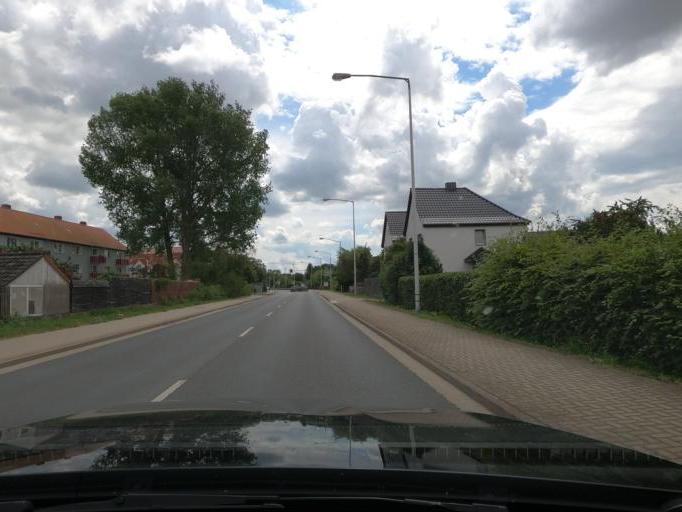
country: DE
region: Lower Saxony
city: Sehnde
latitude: 52.3228
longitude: 9.9537
